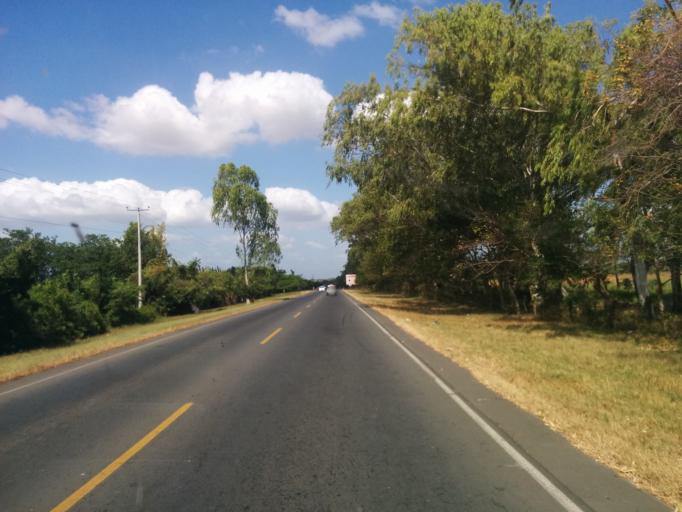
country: NI
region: Masaya
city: Nindiri
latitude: 12.0095
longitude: -86.1040
